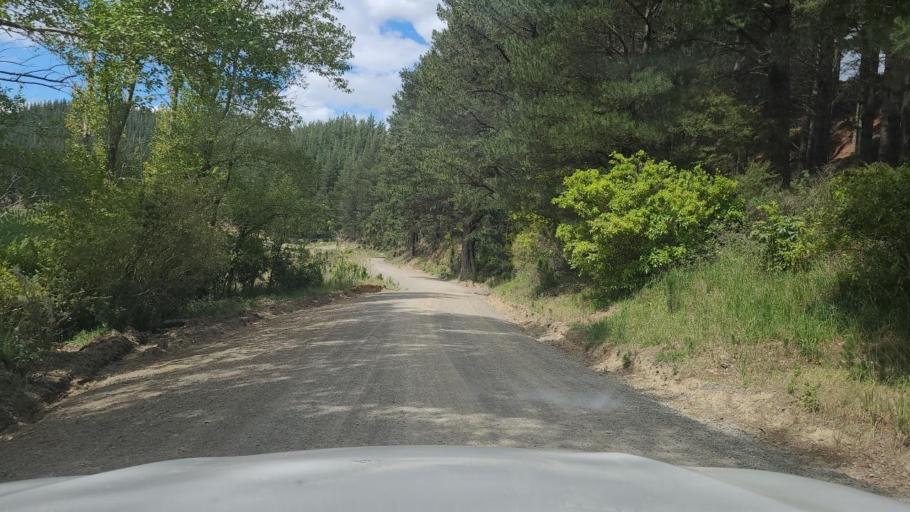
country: NZ
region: Hawke's Bay
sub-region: Napier City
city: Napier
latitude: -39.2523
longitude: 176.7325
